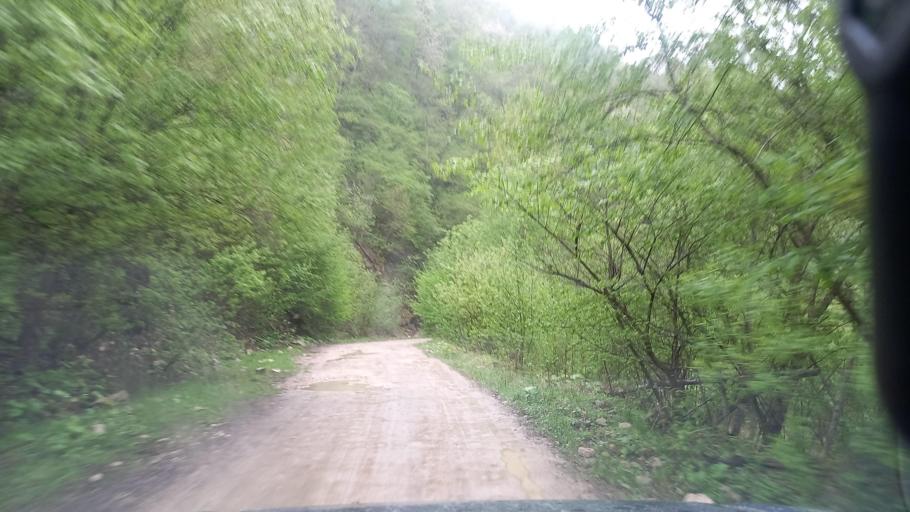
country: RU
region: Kabardino-Balkariya
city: Gundelen
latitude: 43.5800
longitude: 43.1121
